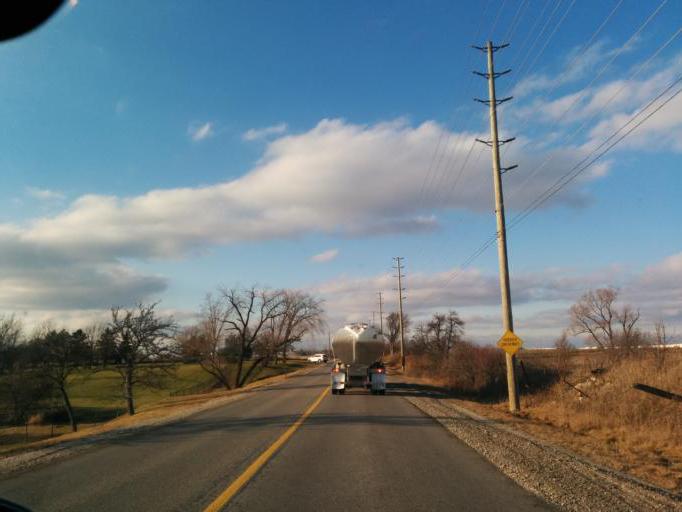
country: CA
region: Ontario
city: Oakville
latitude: 43.5126
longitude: -79.7033
